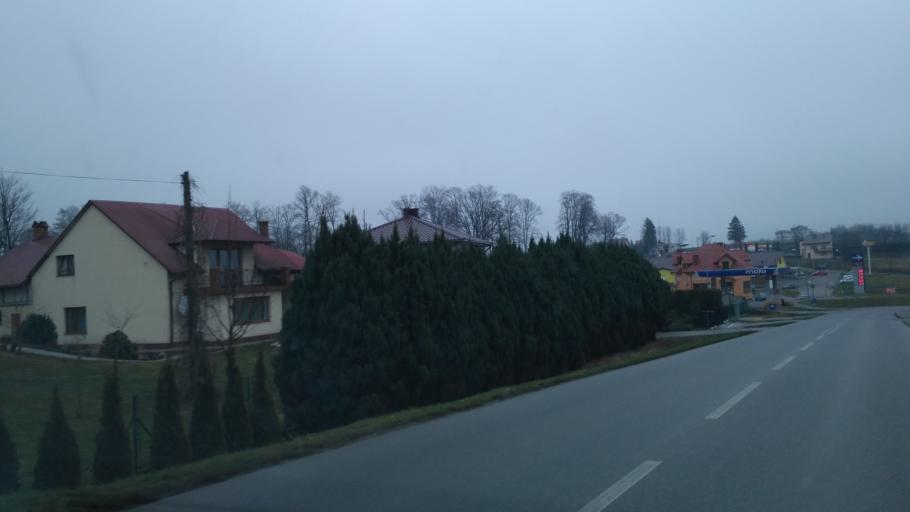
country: PL
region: Subcarpathian Voivodeship
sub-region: Powiat jaroslawski
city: Pruchnik
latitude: 49.9087
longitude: 22.5089
